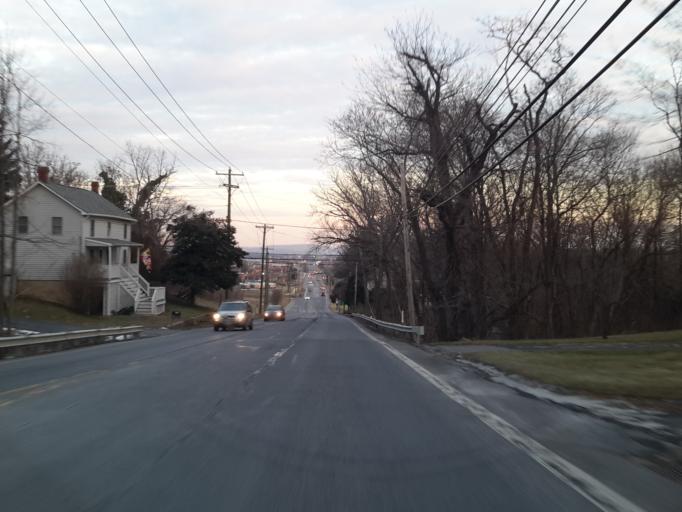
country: US
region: Maryland
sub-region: Frederick County
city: Braddock Heights
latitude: 39.4205
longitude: -77.4720
